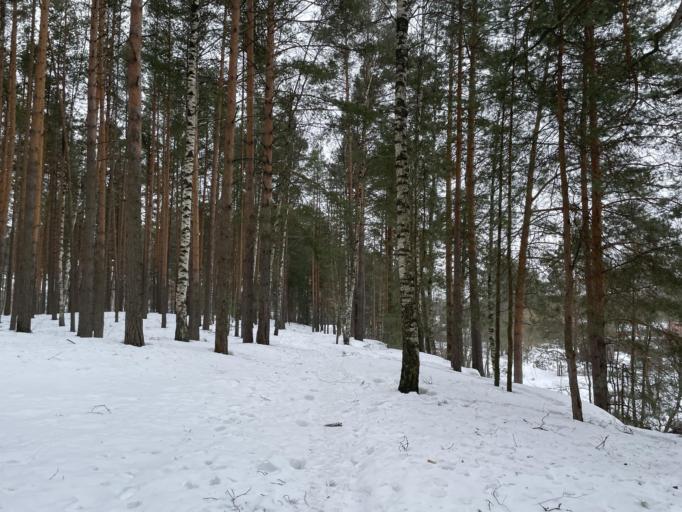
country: RU
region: Vladimir
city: Pokrov
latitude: 55.9389
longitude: 39.2373
